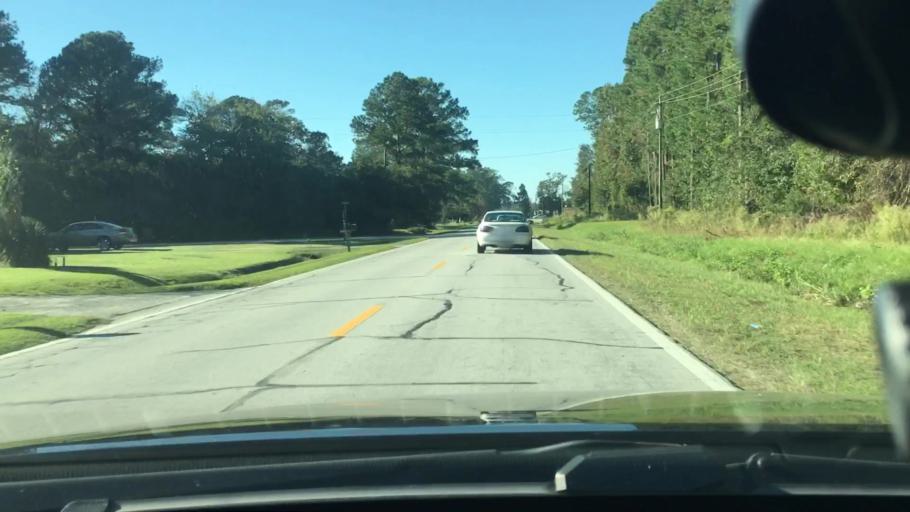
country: US
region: North Carolina
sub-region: Craven County
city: Vanceboro
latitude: 35.2279
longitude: -77.1343
